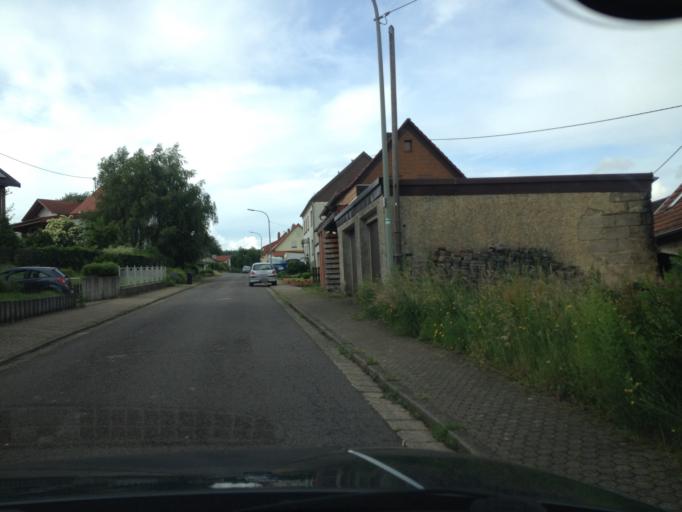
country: DE
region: Saarland
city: Marpingen
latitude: 49.4748
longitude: 7.0715
